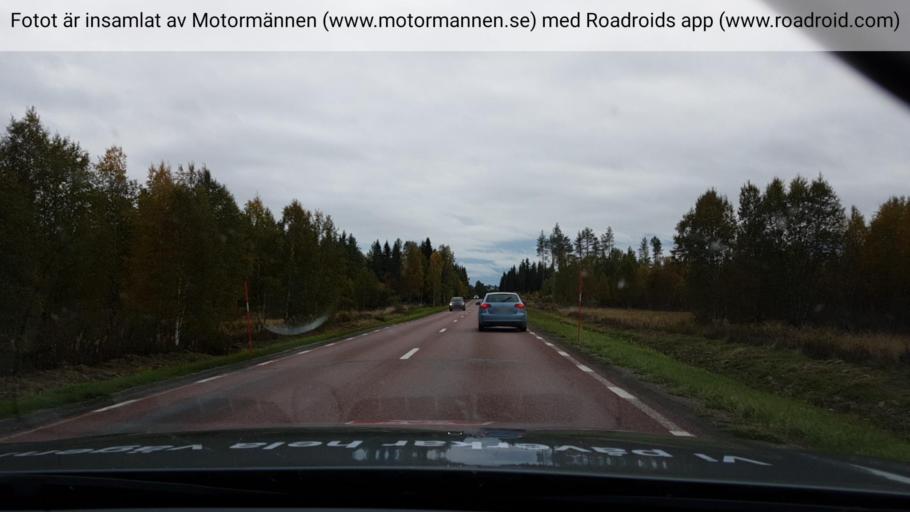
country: SE
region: Jaemtland
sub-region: Stroemsunds Kommun
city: Stroemsund
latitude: 63.7544
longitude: 15.4969
